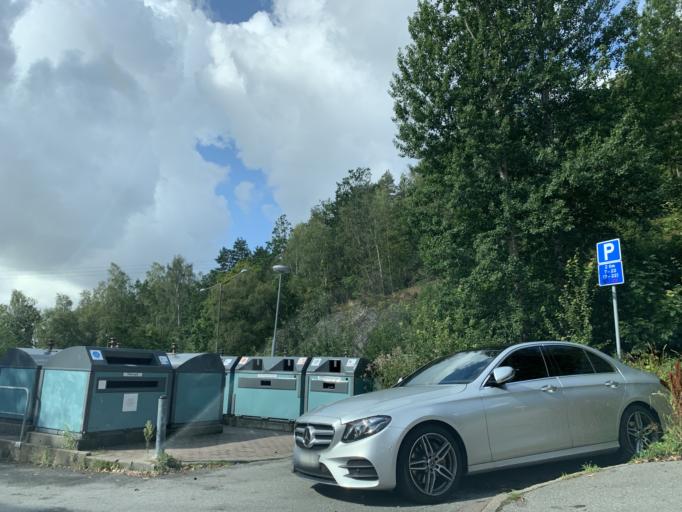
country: SE
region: Vaestra Goetaland
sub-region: Goteborg
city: Eriksbo
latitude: 57.7451
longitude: 12.0271
